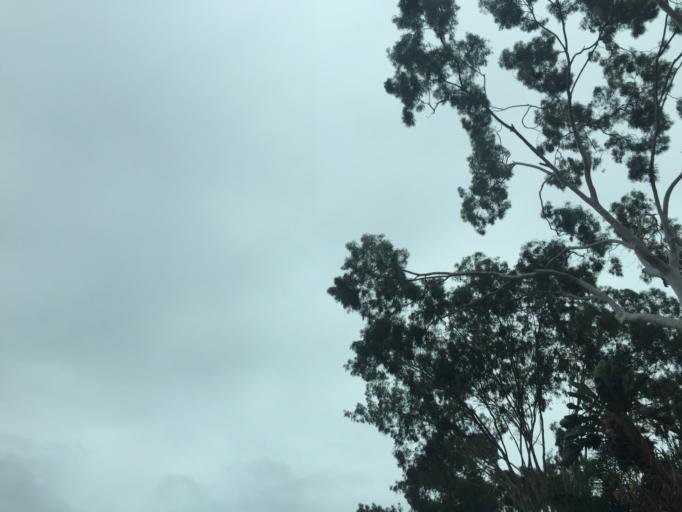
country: US
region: California
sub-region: San Diego County
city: La Jolla
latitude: 32.7901
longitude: -117.2380
